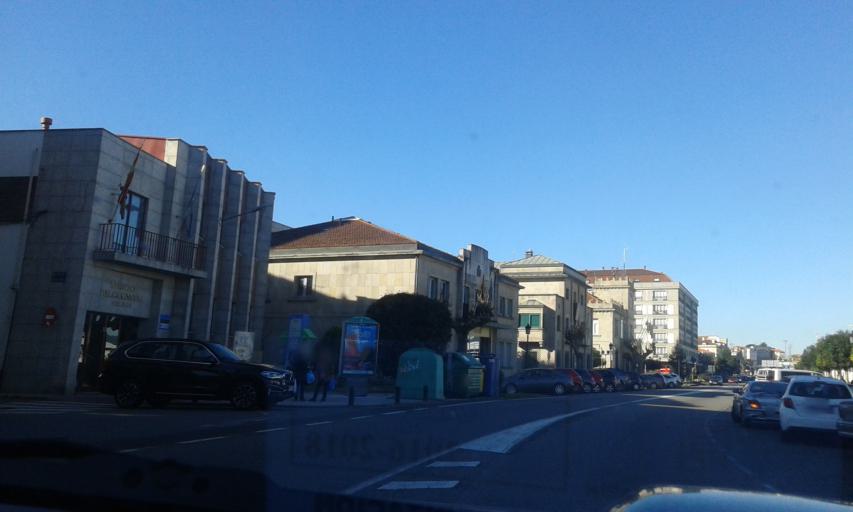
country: ES
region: Galicia
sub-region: Provincia de Pontevedra
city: Marin
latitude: 42.3928
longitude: -8.6973
